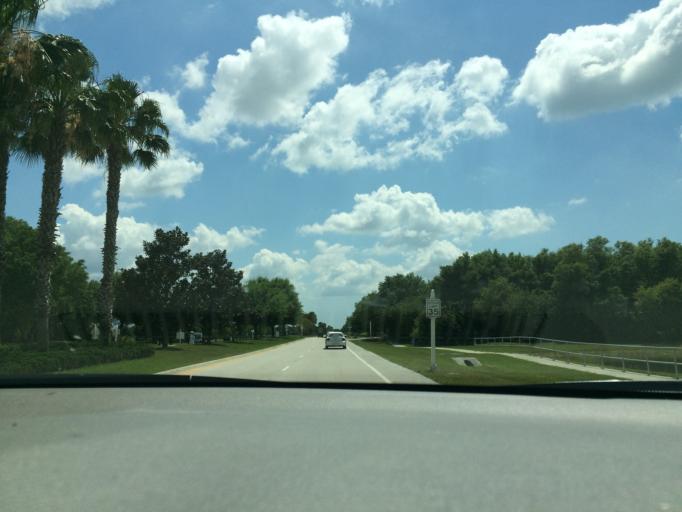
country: US
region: Florida
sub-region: Sarasota County
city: The Meadows
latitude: 27.3952
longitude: -82.3985
